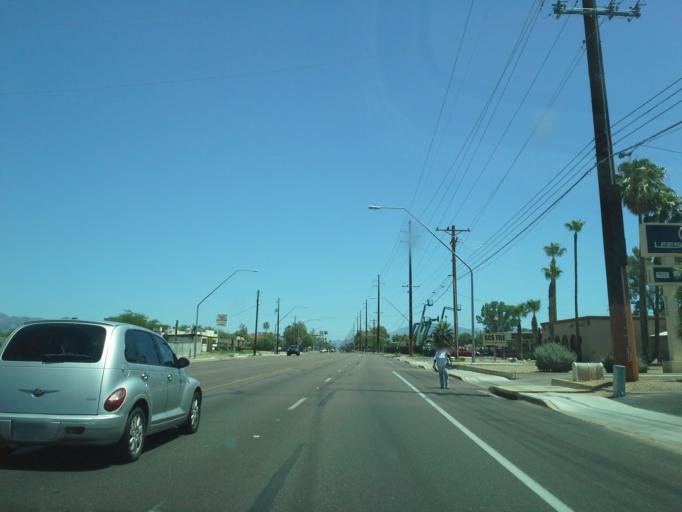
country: US
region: Arizona
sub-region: Pima County
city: Catalina Foothills
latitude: 32.2648
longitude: -110.9593
